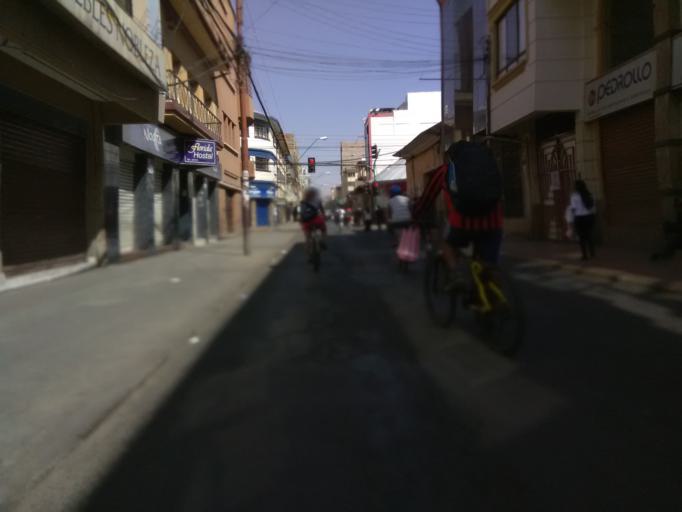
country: BO
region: Cochabamba
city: Cochabamba
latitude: -17.3967
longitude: -66.1547
